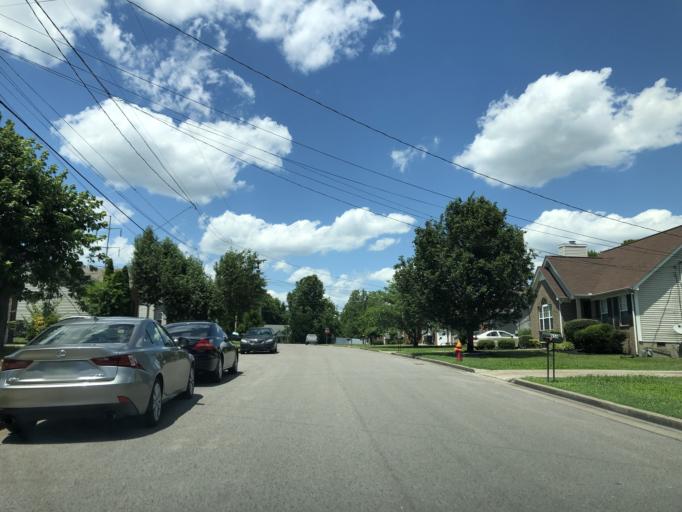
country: US
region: Tennessee
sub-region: Davidson County
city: Nashville
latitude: 36.1854
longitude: -86.7200
